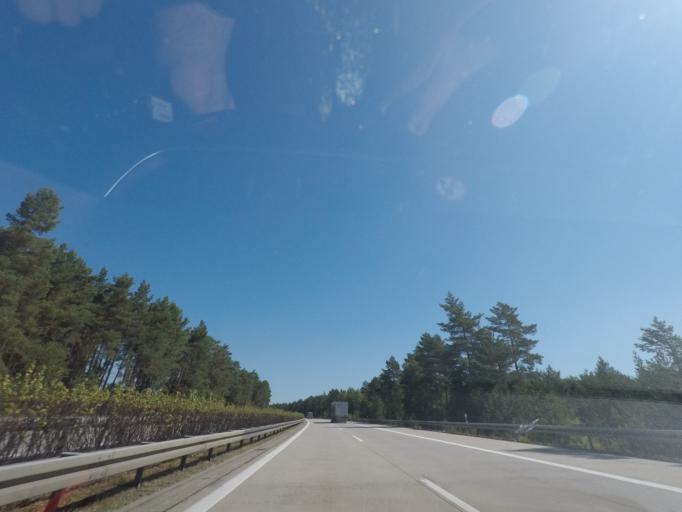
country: DE
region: Brandenburg
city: Kroppen
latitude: 51.4125
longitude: 13.8036
